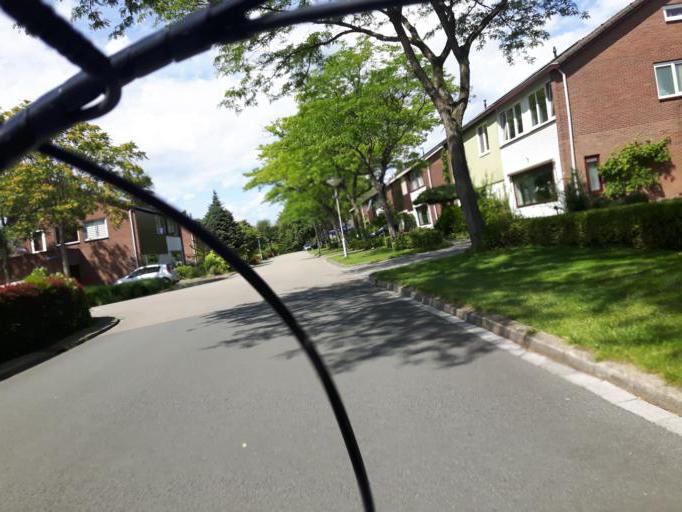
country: NL
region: Zeeland
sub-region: Gemeente Goes
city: Goes
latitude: 51.5087
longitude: 3.9051
